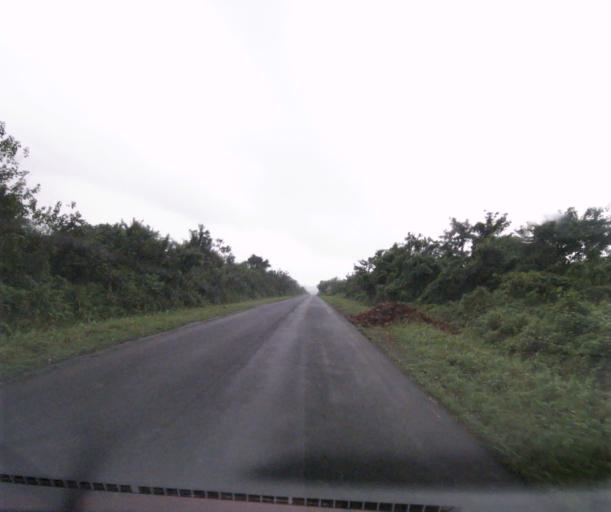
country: CM
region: South-West Province
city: Idenao
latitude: 4.1912
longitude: 9.0035
